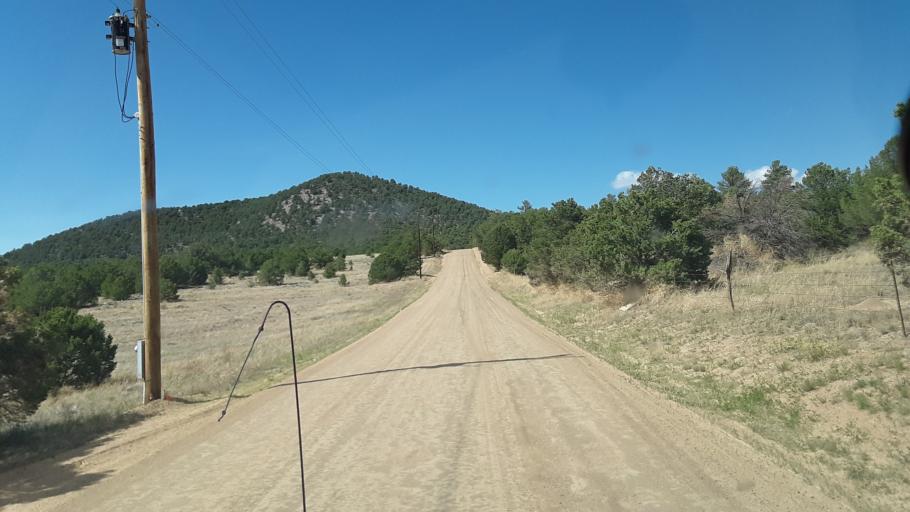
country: US
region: Colorado
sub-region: Custer County
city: Westcliffe
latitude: 38.2932
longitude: -105.4911
